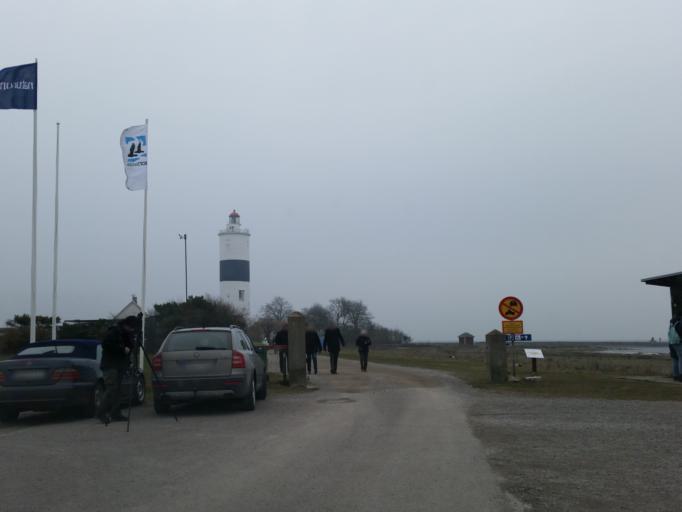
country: SE
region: Kalmar
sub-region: Morbylanga Kommun
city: Moerbylanga
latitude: 56.1981
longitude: 16.3989
